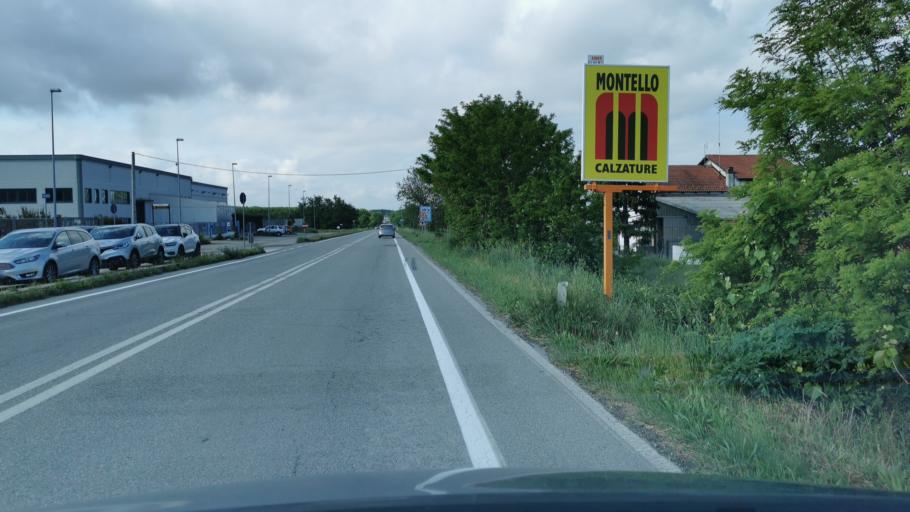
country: IT
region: Piedmont
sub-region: Provincia di Torino
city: Santena
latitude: 44.9539
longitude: 7.7862
